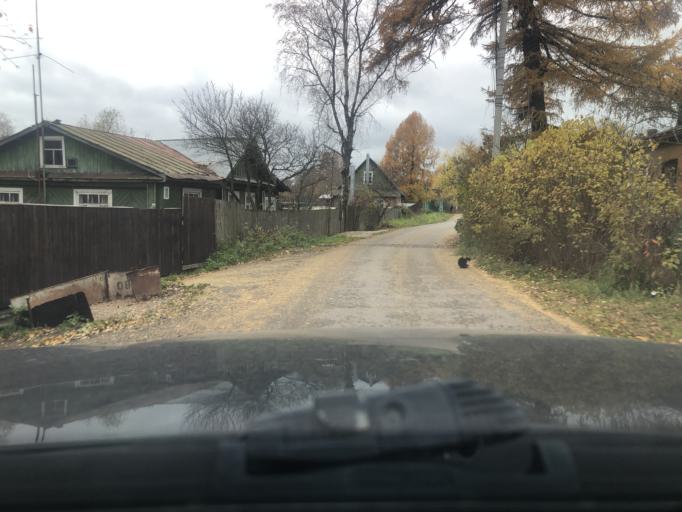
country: RU
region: Moskovskaya
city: Sergiyev Posad
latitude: 56.3113
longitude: 38.1182
